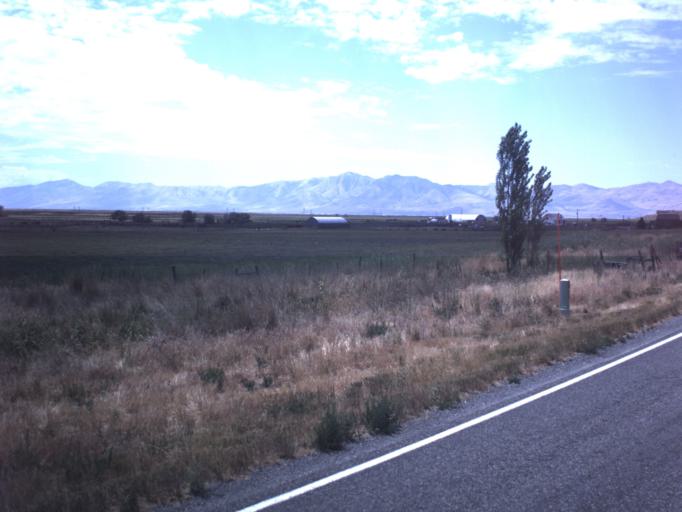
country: US
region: Utah
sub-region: Box Elder County
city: Tremonton
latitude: 41.6261
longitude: -112.3382
